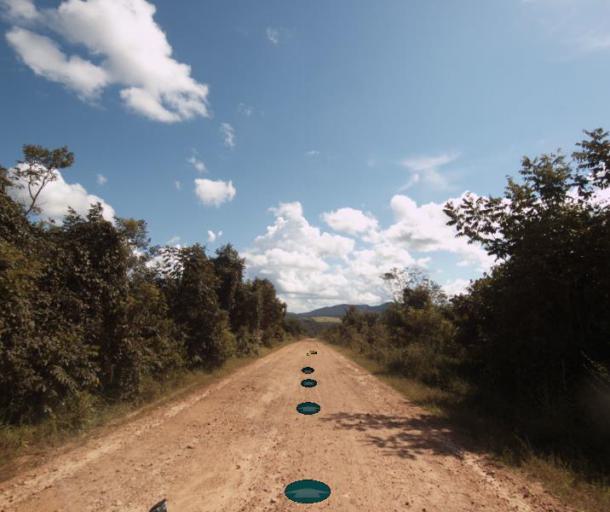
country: BR
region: Goias
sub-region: Pirenopolis
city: Pirenopolis
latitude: -15.7876
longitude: -49.0658
